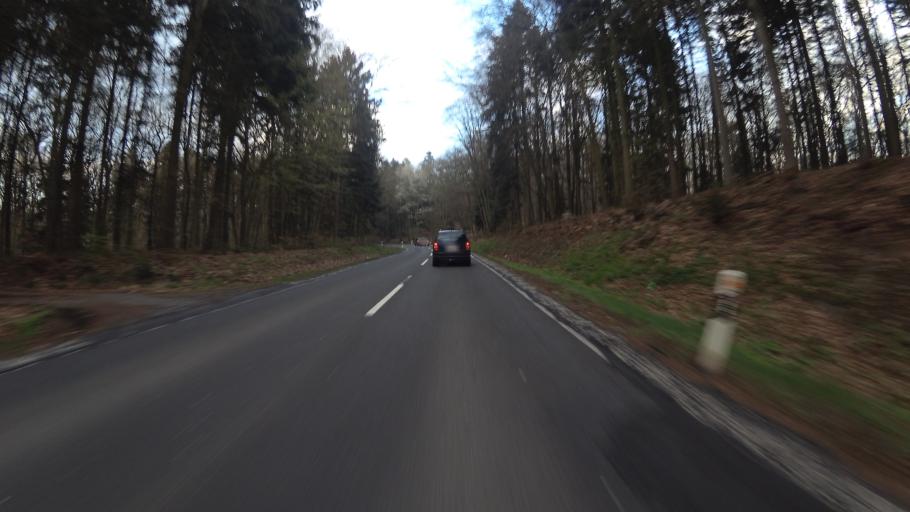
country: DE
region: Rheinland-Pfalz
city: Monzelfeld
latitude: 49.8936
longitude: 7.0417
